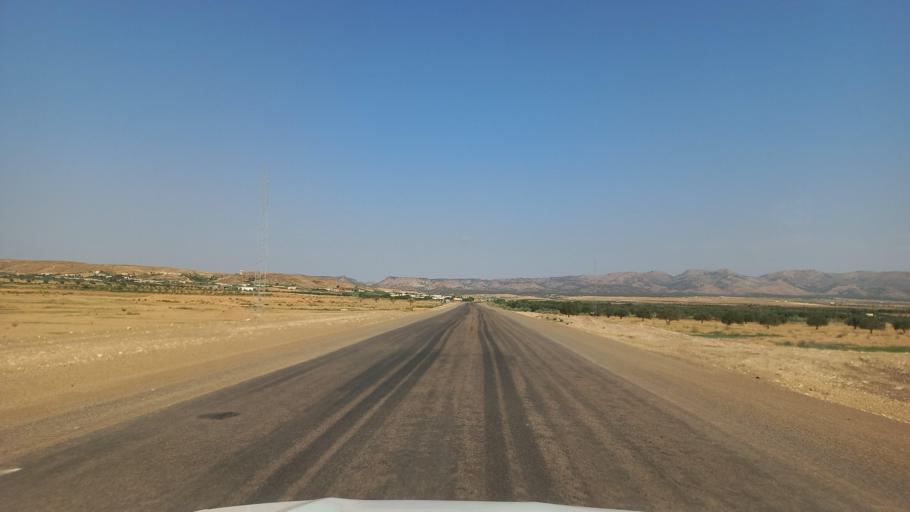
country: TN
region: Al Qasrayn
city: Sbiba
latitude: 35.3740
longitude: 9.0343
